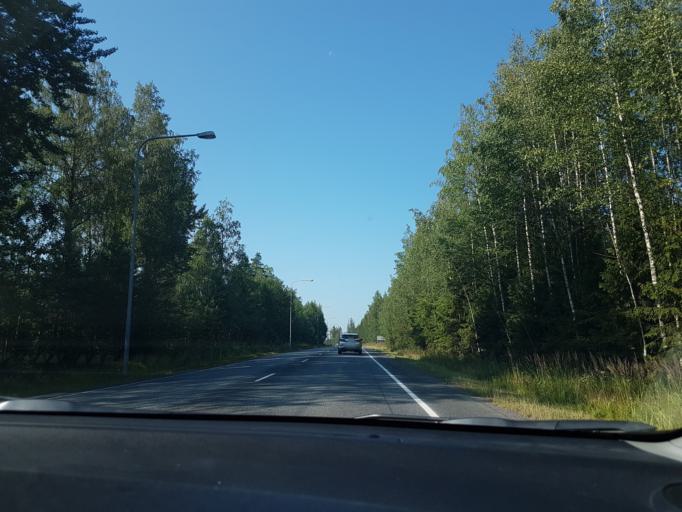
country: FI
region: Uusimaa
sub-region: Helsinki
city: Tuusula
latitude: 60.3815
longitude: 25.0618
